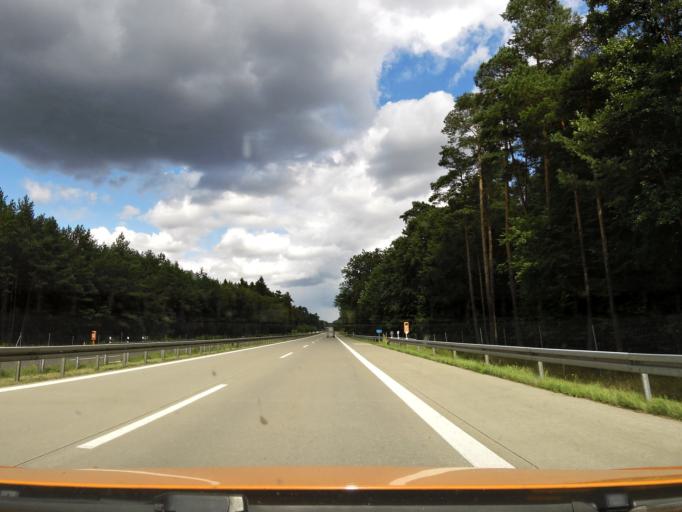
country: DE
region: Brandenburg
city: Althuttendorf
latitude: 53.0254
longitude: 13.8294
